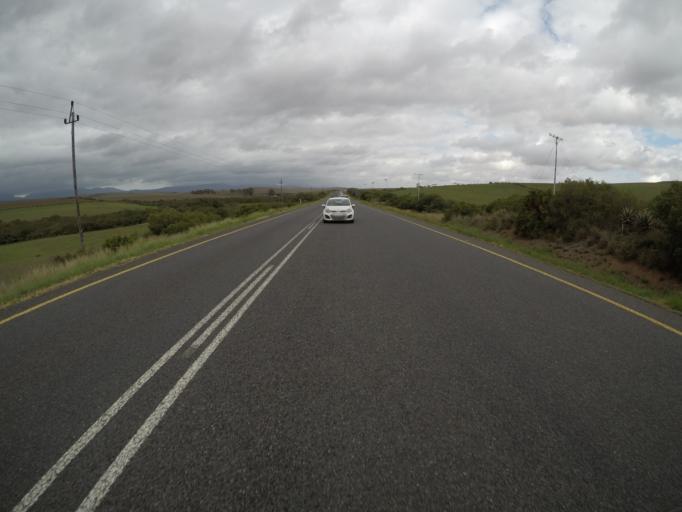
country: ZA
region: Western Cape
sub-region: Eden District Municipality
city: Riversdale
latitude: -34.1152
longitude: 20.8853
